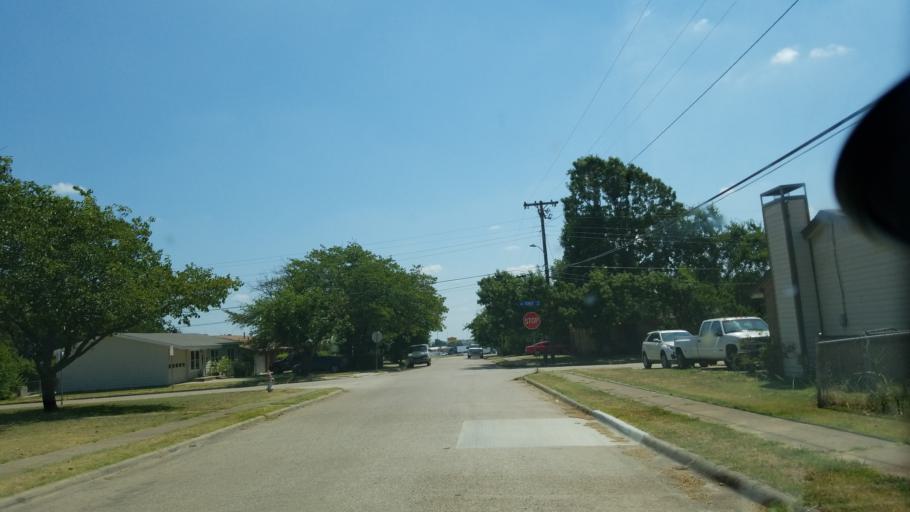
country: US
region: Texas
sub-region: Dallas County
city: Duncanville
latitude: 32.6608
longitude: -96.8969
